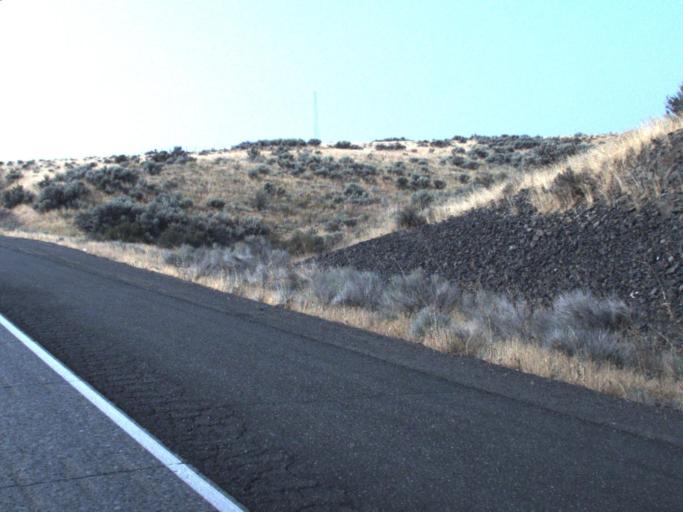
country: US
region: Washington
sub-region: Yakima County
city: Terrace Heights
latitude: 46.7754
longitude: -120.3757
